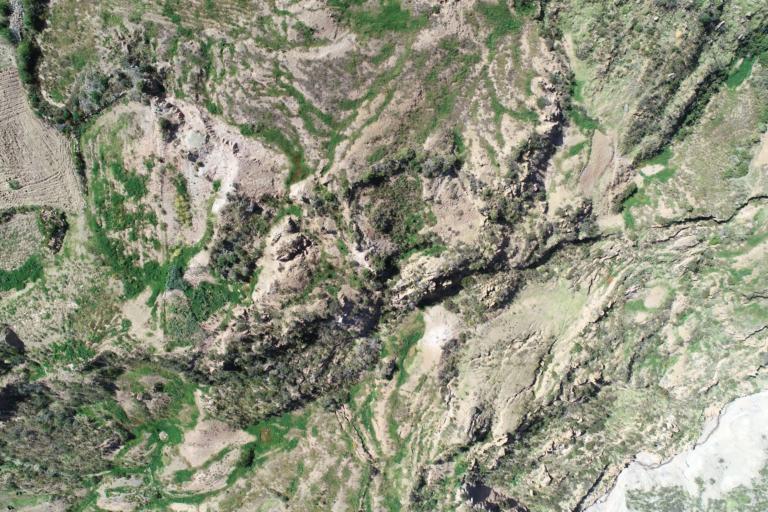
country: BO
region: La Paz
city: La Paz
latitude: -16.5575
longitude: -67.9865
